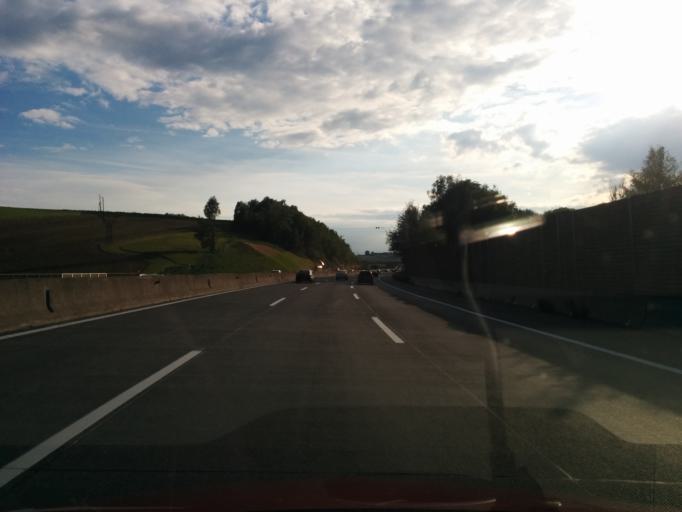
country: AT
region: Lower Austria
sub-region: Politischer Bezirk Melk
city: Erlauf
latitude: 48.1730
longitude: 15.1823
